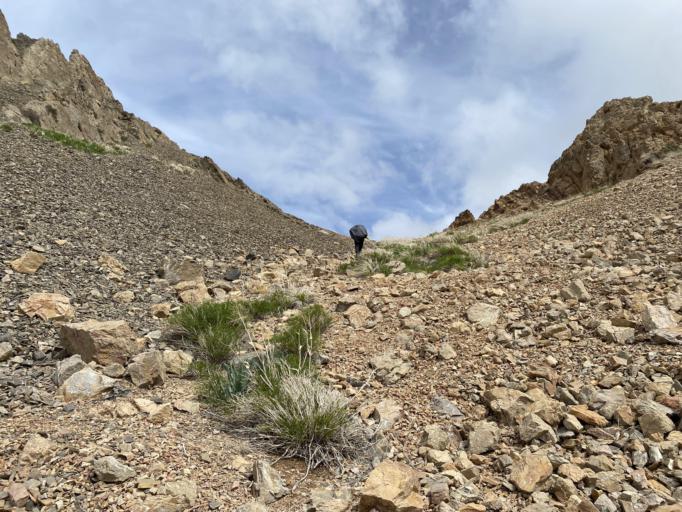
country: KZ
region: Ongtustik Qazaqstan
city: Ashchysay
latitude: 43.7473
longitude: 68.8277
